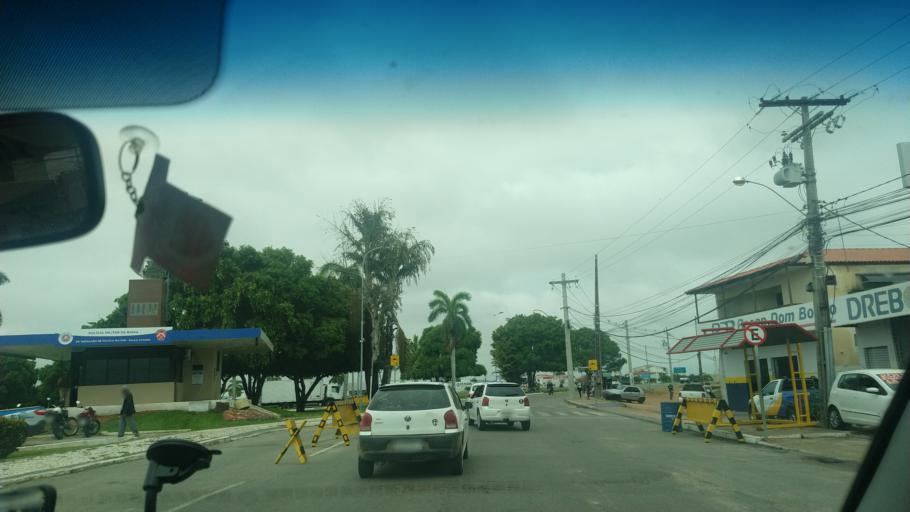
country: BR
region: Bahia
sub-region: Paulo Afonso
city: Paulo Afonso
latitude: -9.4012
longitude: -38.2369
